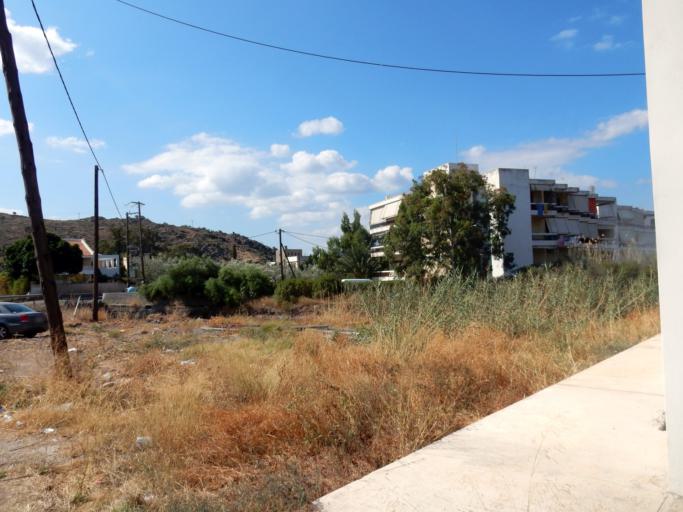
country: GR
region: Attica
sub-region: Nomos Piraios
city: Kypseli
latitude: 37.7175
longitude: 23.4629
